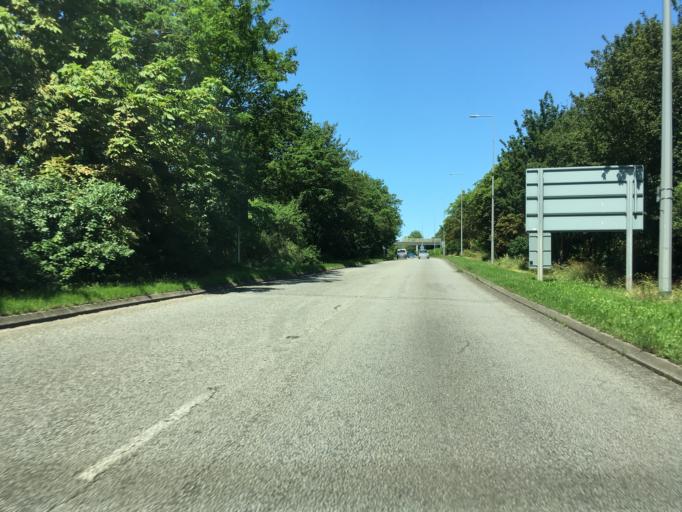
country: GB
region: England
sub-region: Milton Keynes
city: Milton Keynes
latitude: 52.0372
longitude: -0.7375
